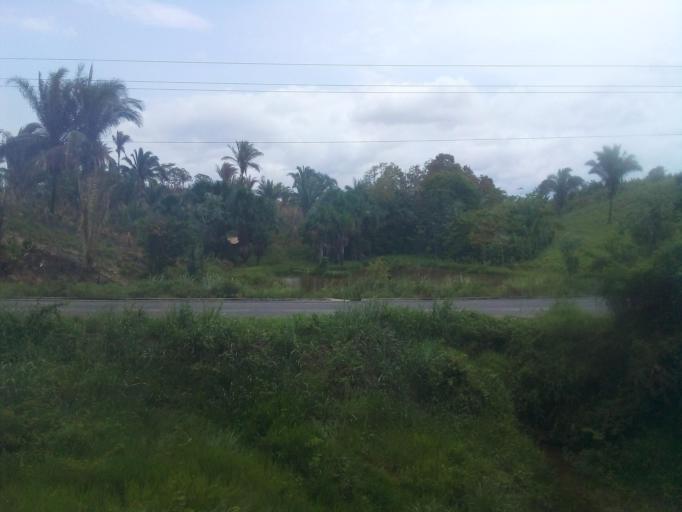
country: BR
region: Maranhao
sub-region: Santa Ines
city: Santa Ines
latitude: -3.7001
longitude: -45.9699
